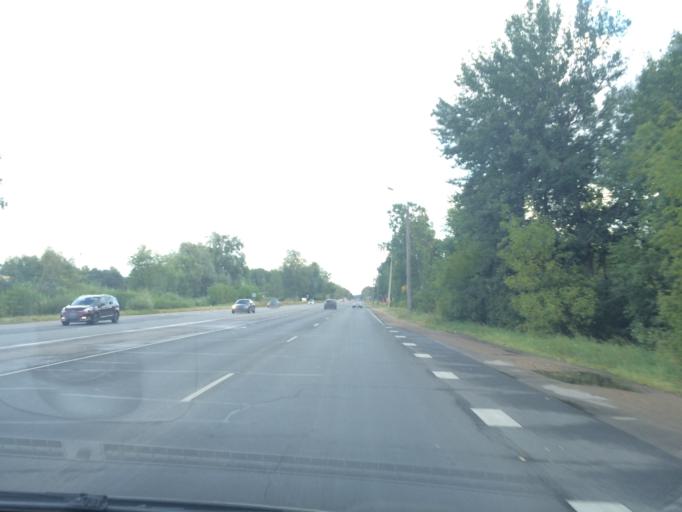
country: LV
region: Kekava
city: Kekava
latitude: 56.8815
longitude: 24.2472
